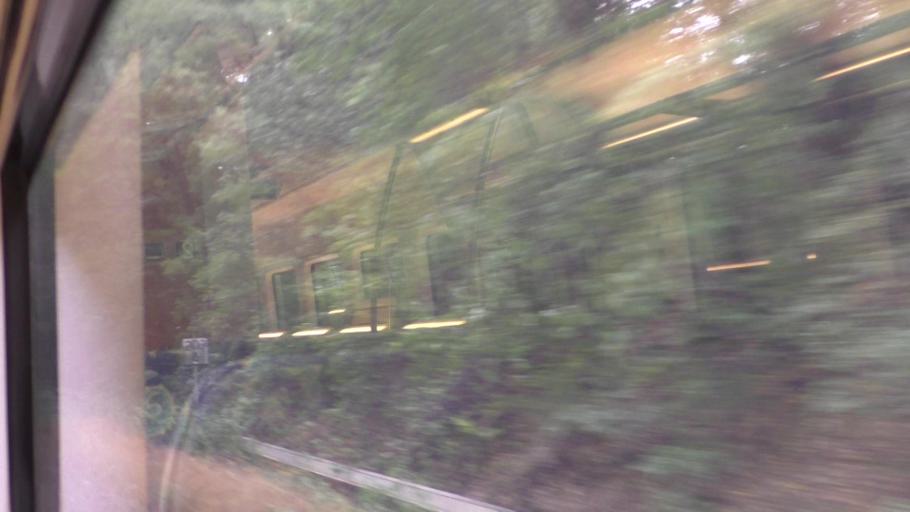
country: DE
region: Saxony
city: Goerlitz
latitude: 51.1783
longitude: 14.9667
